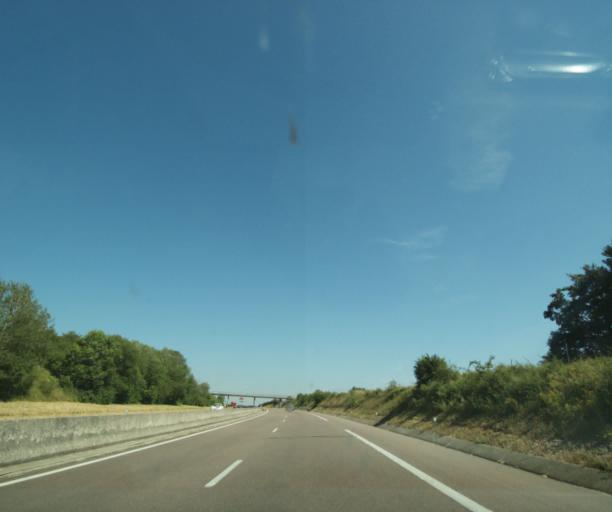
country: FR
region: Lorraine
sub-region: Departement des Vosges
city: Chatenois
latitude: 48.4010
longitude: 5.8806
